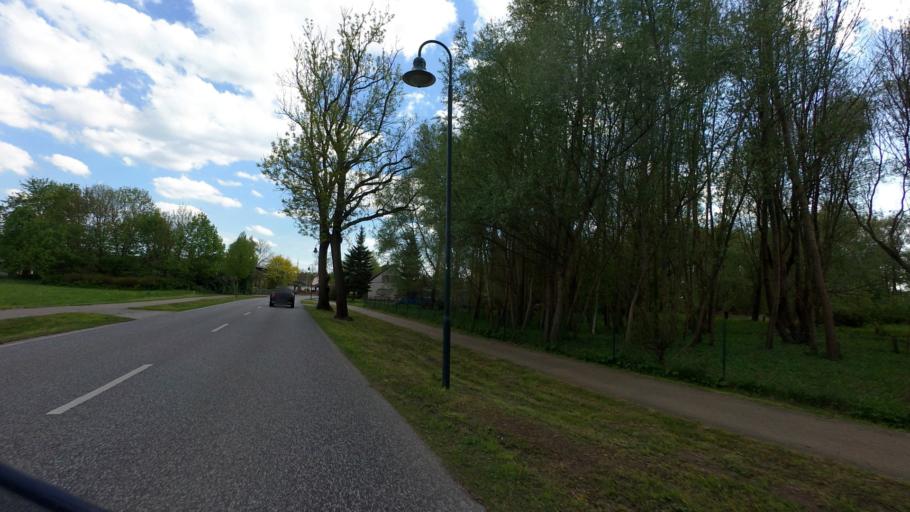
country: DE
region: Brandenburg
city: Liebenwalde
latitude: 52.8641
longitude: 13.3968
